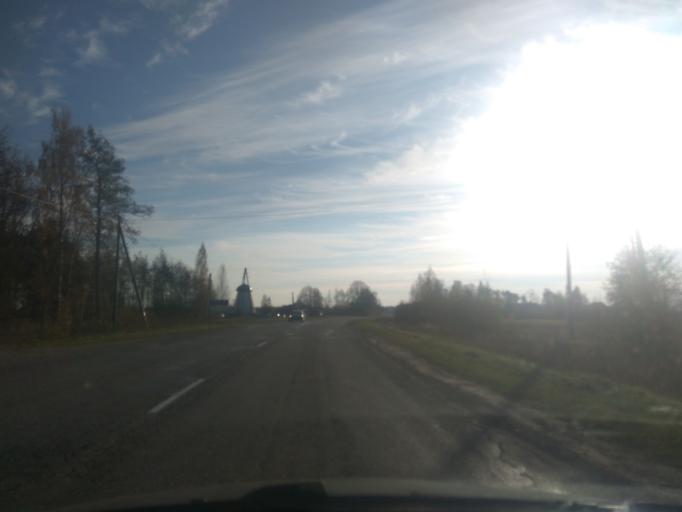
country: LV
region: Ventspils
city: Ventspils
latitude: 57.3432
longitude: 21.5693
